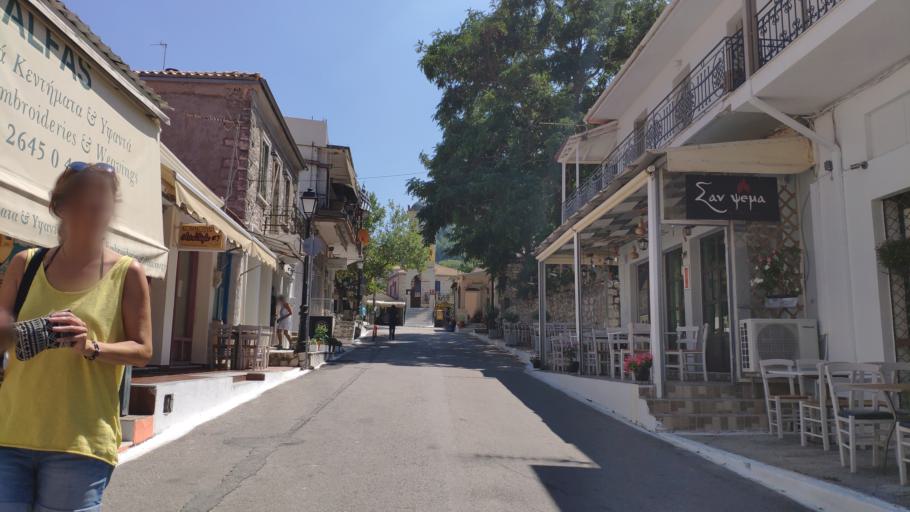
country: GR
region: Ionian Islands
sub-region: Lefkada
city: Nidri
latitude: 38.7595
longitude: 20.6487
